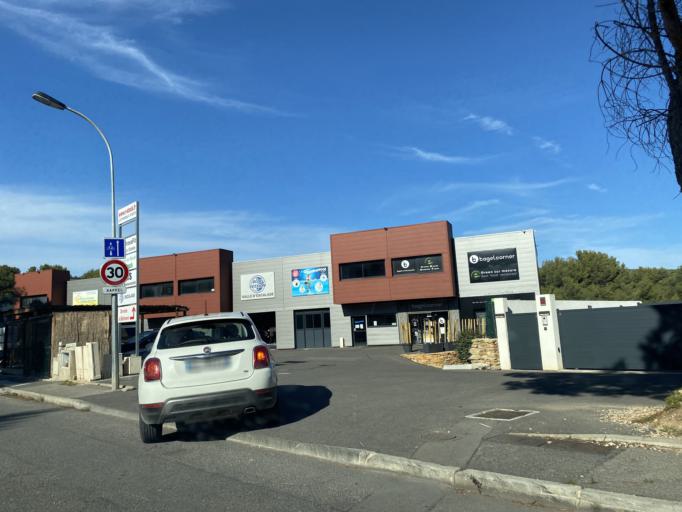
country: FR
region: Provence-Alpes-Cote d'Azur
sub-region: Departement des Bouches-du-Rhone
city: Ceyreste
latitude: 43.2063
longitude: 5.6088
